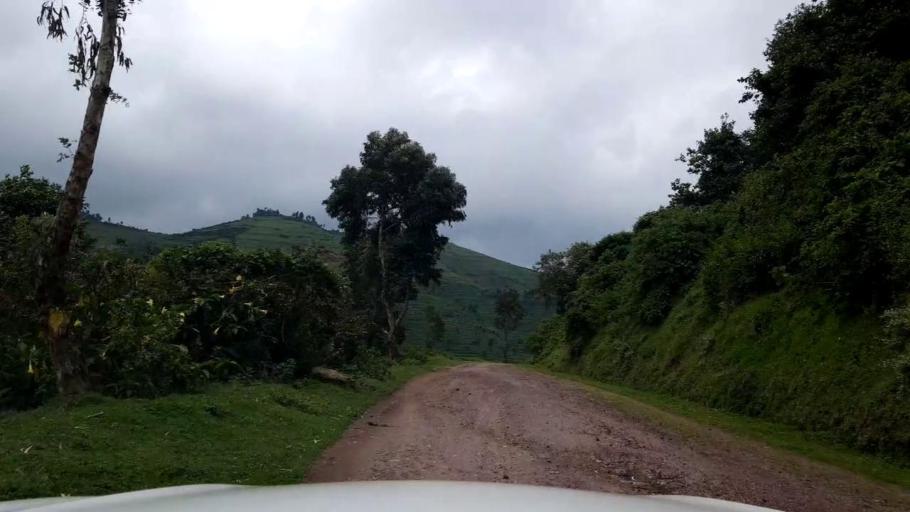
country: RW
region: Western Province
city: Gisenyi
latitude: -1.6650
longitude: 29.4180
